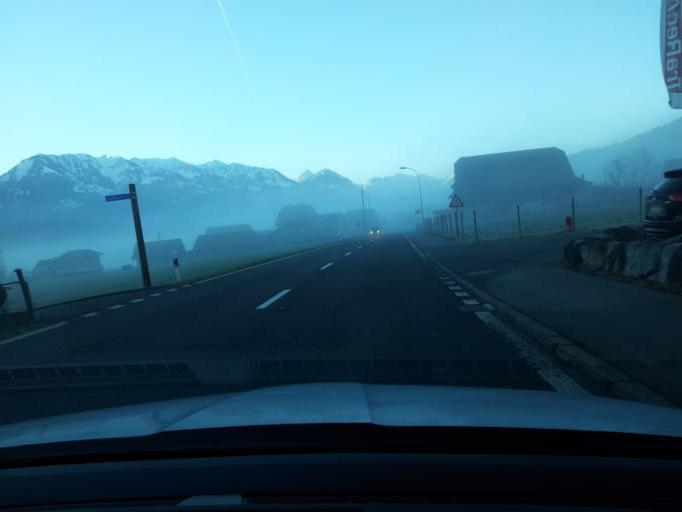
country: CH
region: Obwalden
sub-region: Obwalden
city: Alpnach
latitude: 46.9271
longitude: 8.2665
